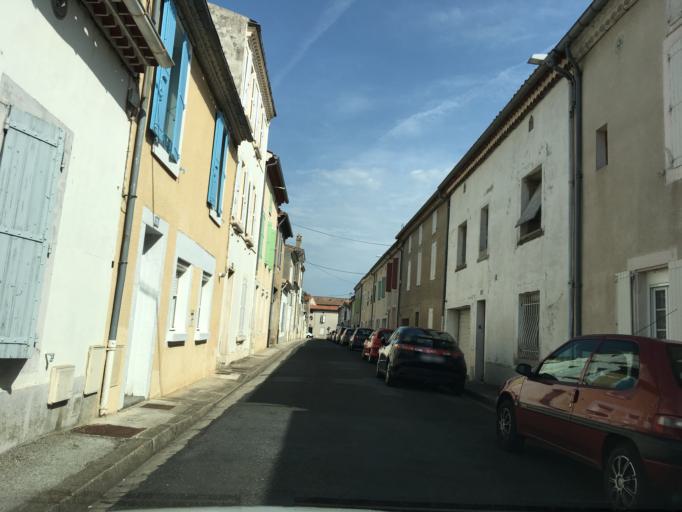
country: FR
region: Midi-Pyrenees
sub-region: Departement du Tarn
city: Castres
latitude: 43.6082
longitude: 2.2459
